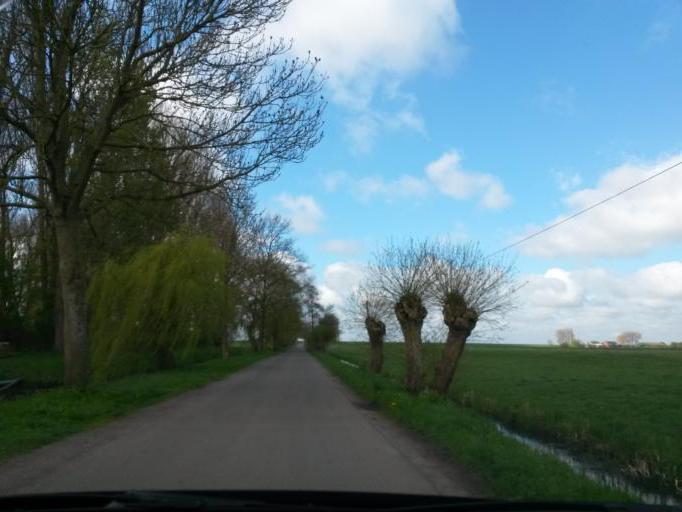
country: DE
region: Schleswig-Holstein
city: Wedel
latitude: 53.5869
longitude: 9.6735
